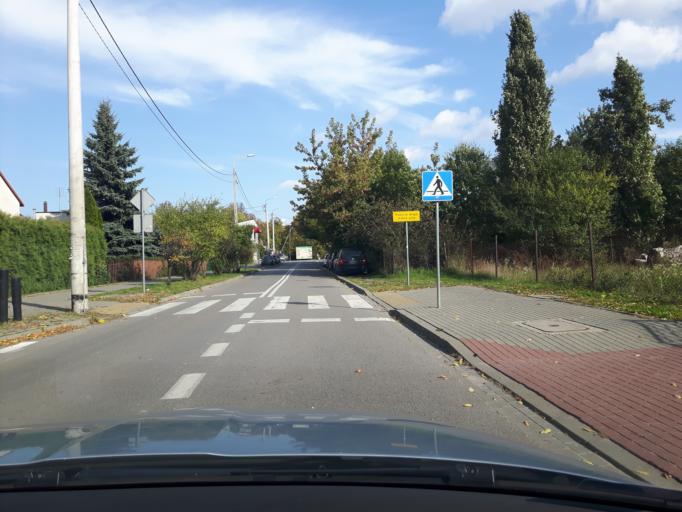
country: PL
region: Masovian Voivodeship
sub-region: Powiat wolominski
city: Zabki
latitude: 52.2916
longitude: 21.1101
